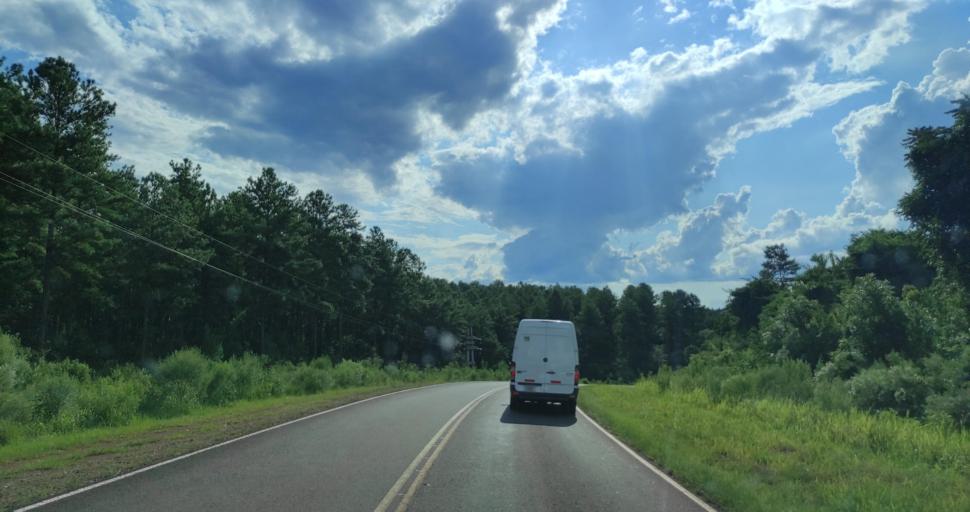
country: AR
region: Misiones
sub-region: Departamento de San Pedro
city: San Pedro
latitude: -26.3493
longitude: -53.9800
